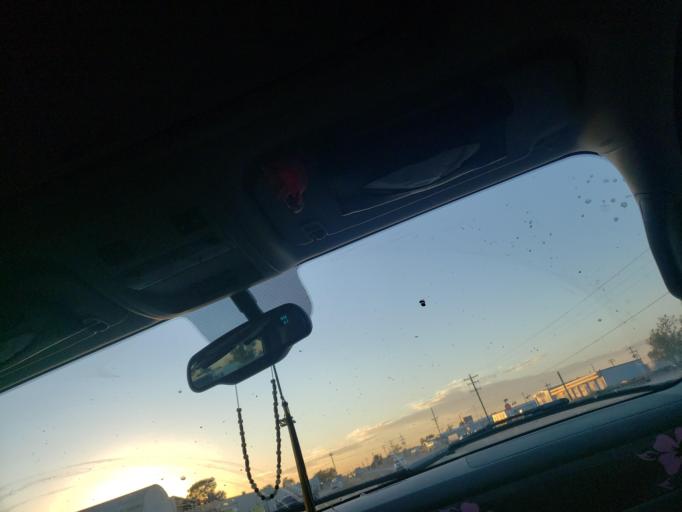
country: US
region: Kansas
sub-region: Finney County
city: Garden City
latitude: 37.9893
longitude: -100.9178
